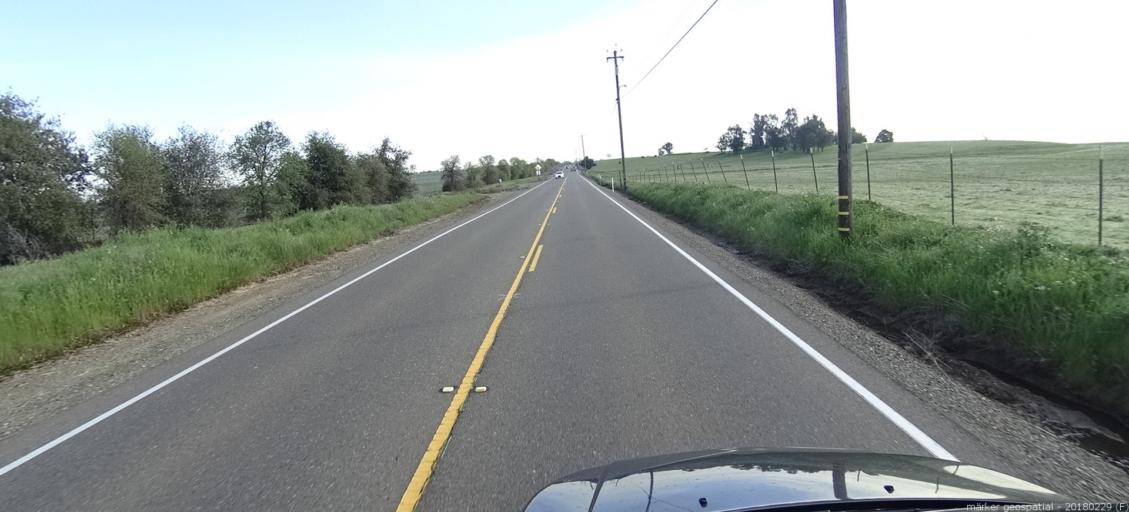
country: US
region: California
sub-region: Sacramento County
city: Rancho Cordova
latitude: 38.5323
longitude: -121.2971
